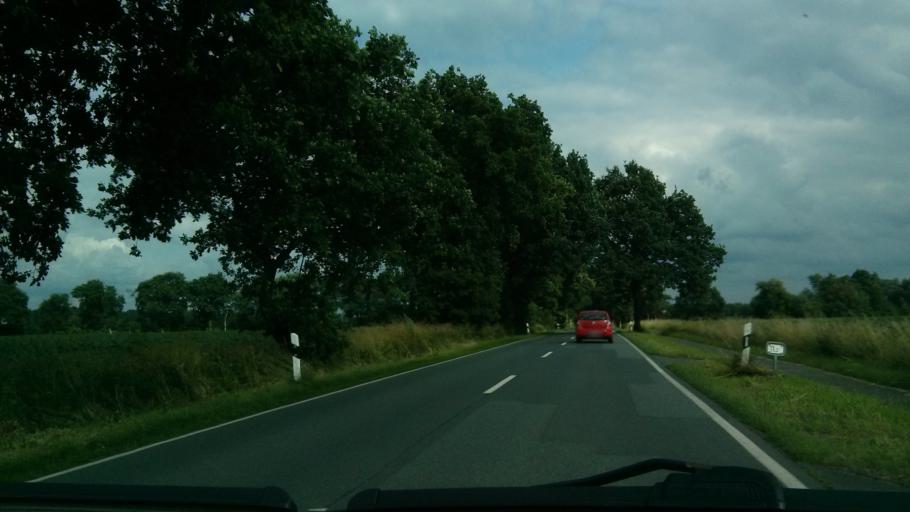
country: DE
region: Lower Saxony
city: Elmlohe
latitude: 53.5148
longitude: 8.7550
